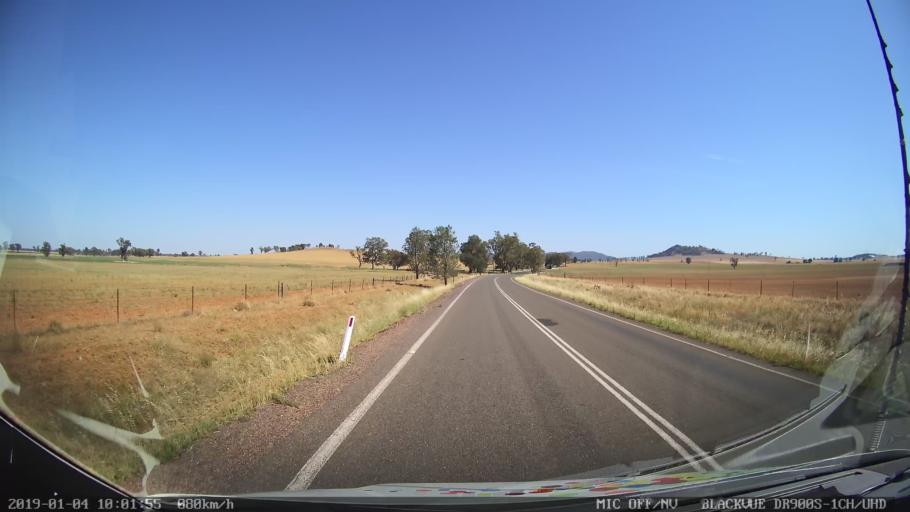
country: AU
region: New South Wales
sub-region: Cabonne
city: Canowindra
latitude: -33.4825
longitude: 148.3668
